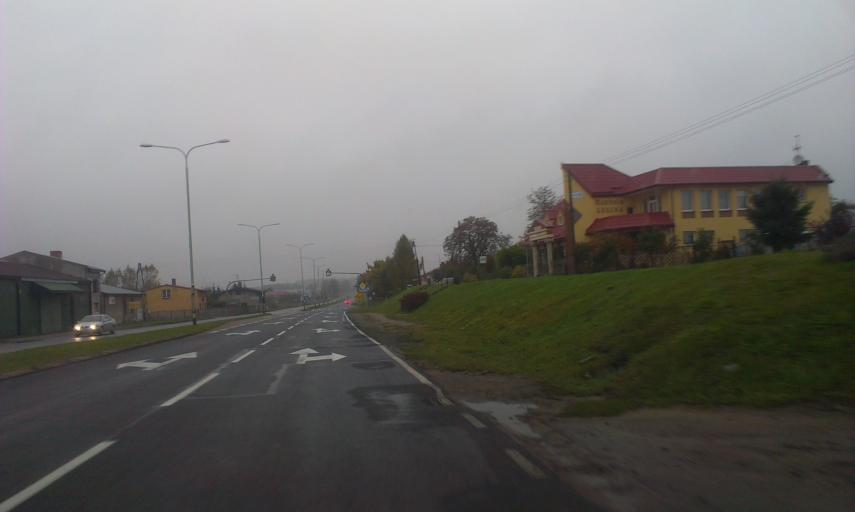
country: PL
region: West Pomeranian Voivodeship
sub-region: Koszalin
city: Koszalin
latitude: 54.1633
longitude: 16.2203
